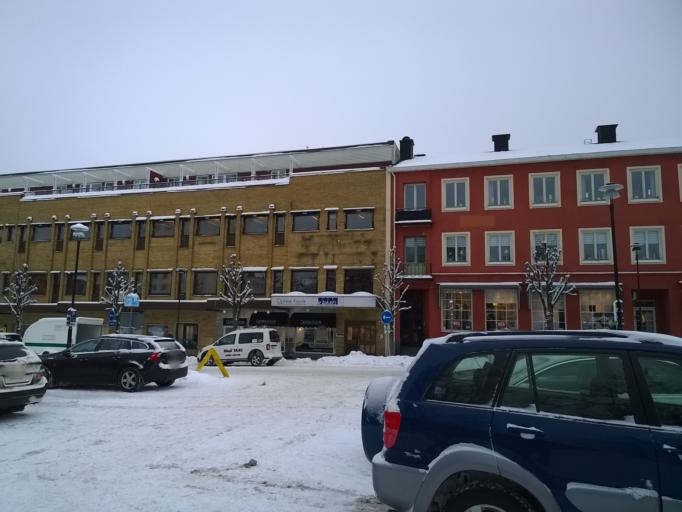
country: SE
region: Joenkoeping
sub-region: Nassjo Kommun
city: Nassjo
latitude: 57.6531
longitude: 14.6967
